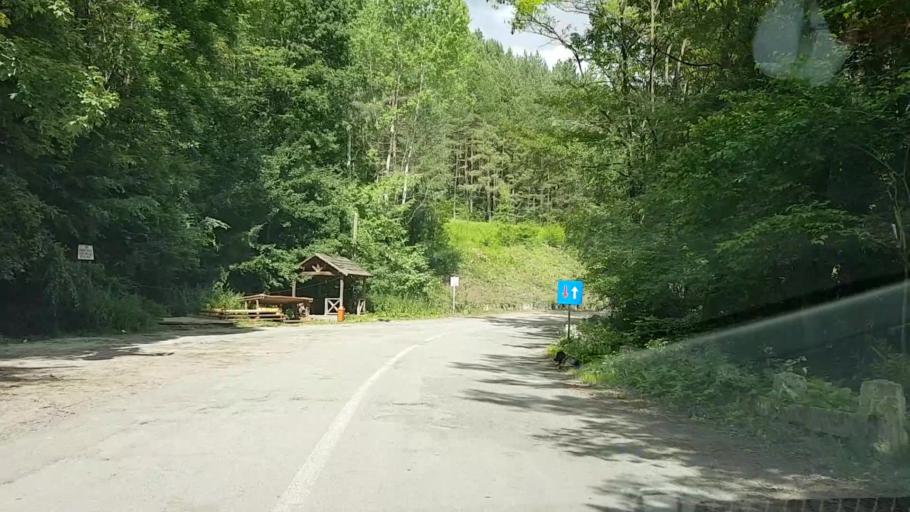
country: RO
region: Neamt
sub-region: Comuna Ceahlau
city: Ceahlau
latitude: 47.0537
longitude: 25.9962
